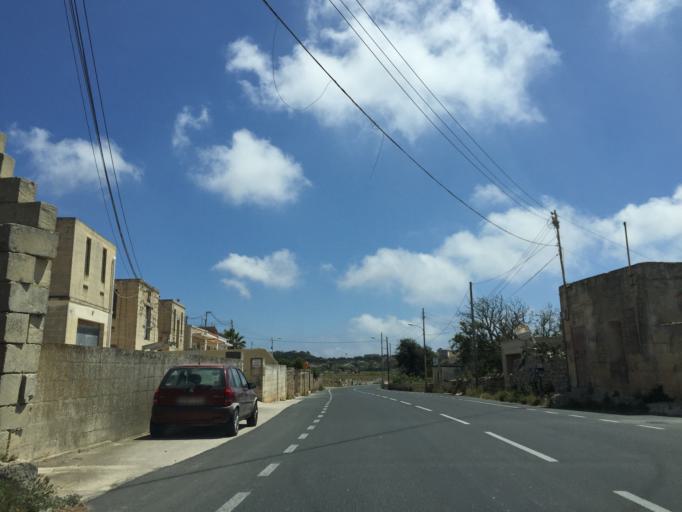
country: MT
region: Dingli
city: Dingli
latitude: 35.8690
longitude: 14.3908
